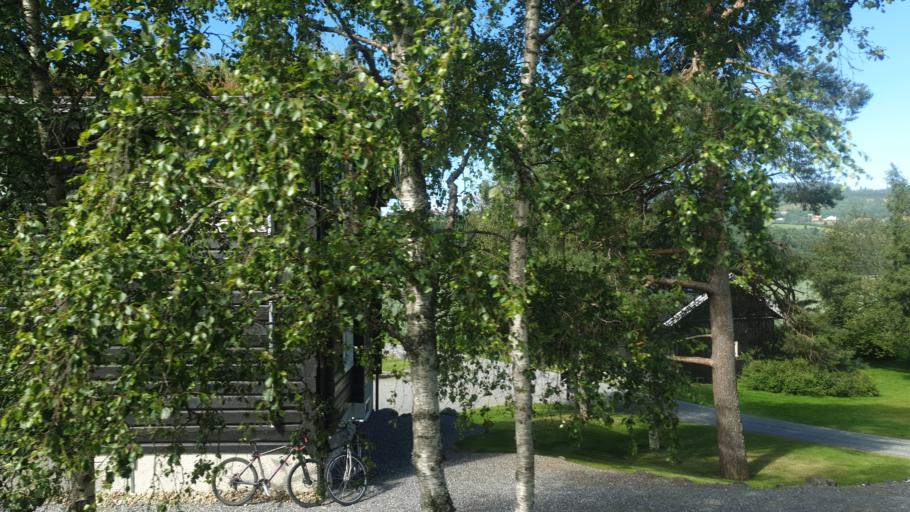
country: NO
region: Sor-Trondelag
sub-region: Orkdal
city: Orkanger
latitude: 63.2719
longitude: 9.8202
